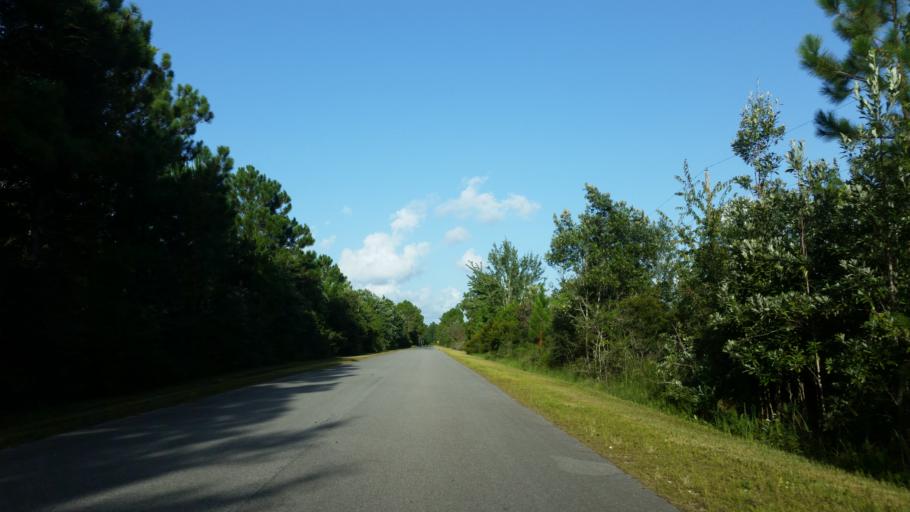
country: US
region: Florida
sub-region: Santa Rosa County
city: Pace
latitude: 30.5346
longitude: -87.1138
